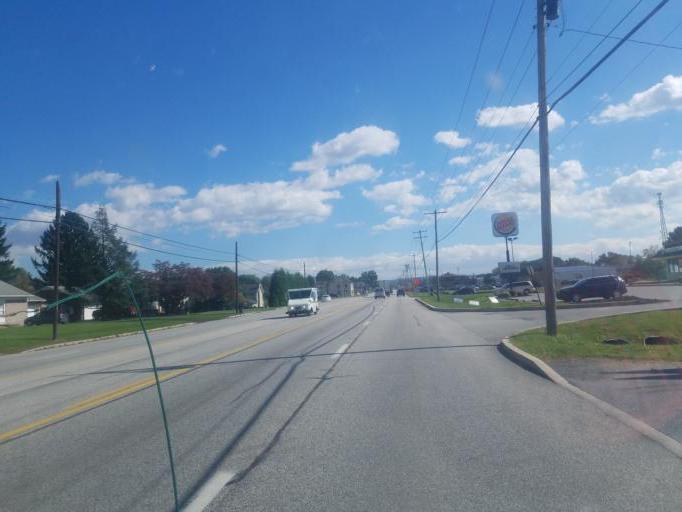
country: US
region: Pennsylvania
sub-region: Franklin County
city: Guilford
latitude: 39.9213
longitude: -77.5962
